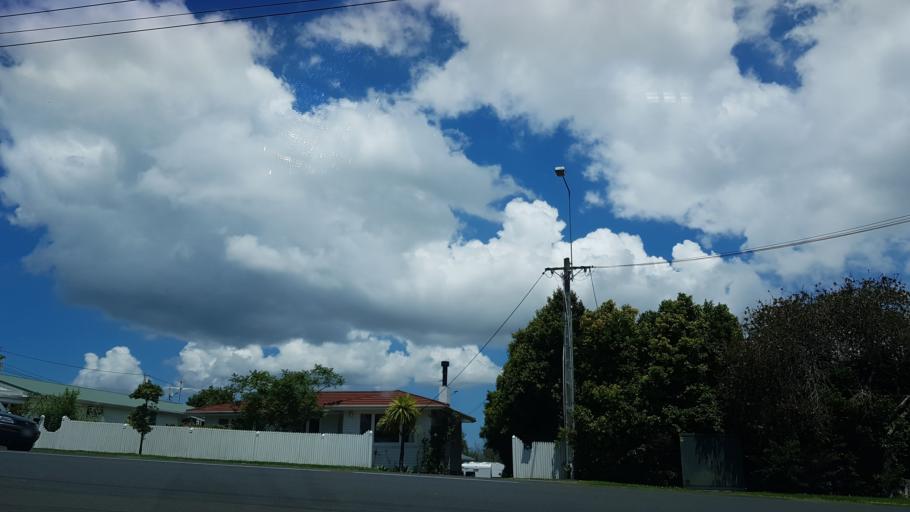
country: NZ
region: Auckland
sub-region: Auckland
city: North Shore
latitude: -36.7953
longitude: 174.6896
